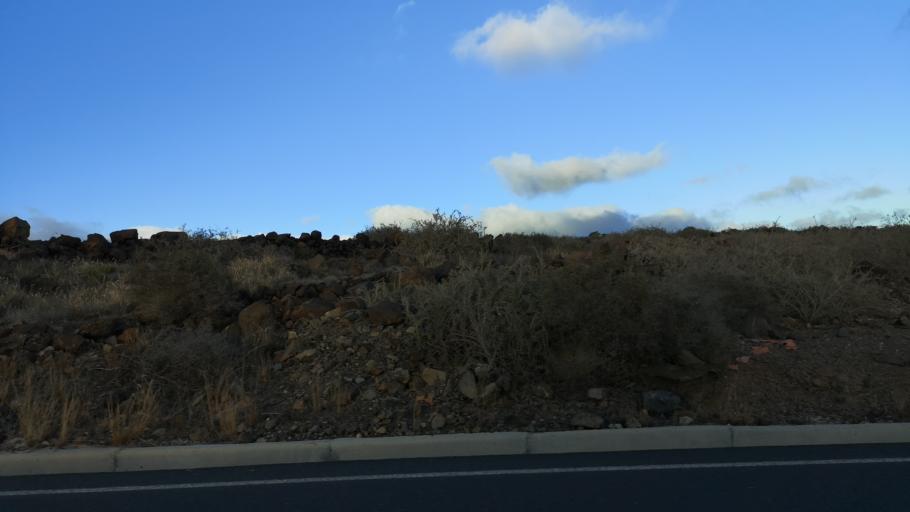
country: ES
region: Canary Islands
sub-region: Provincia de Santa Cruz de Tenerife
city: Alajero
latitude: 28.0338
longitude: -17.2209
